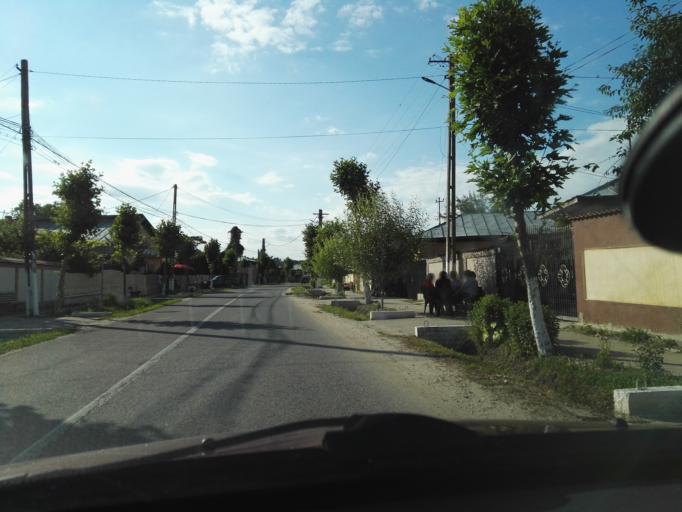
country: RO
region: Giurgiu
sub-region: Comuna Comana
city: Gradistea
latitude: 44.2143
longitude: 26.1591
